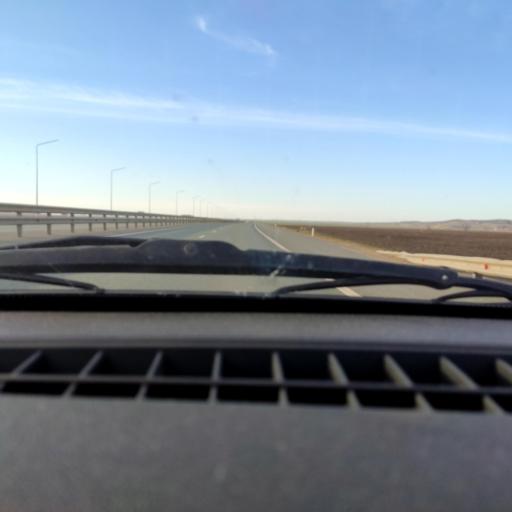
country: RU
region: Bashkortostan
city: Tolbazy
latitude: 54.2097
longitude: 55.8842
